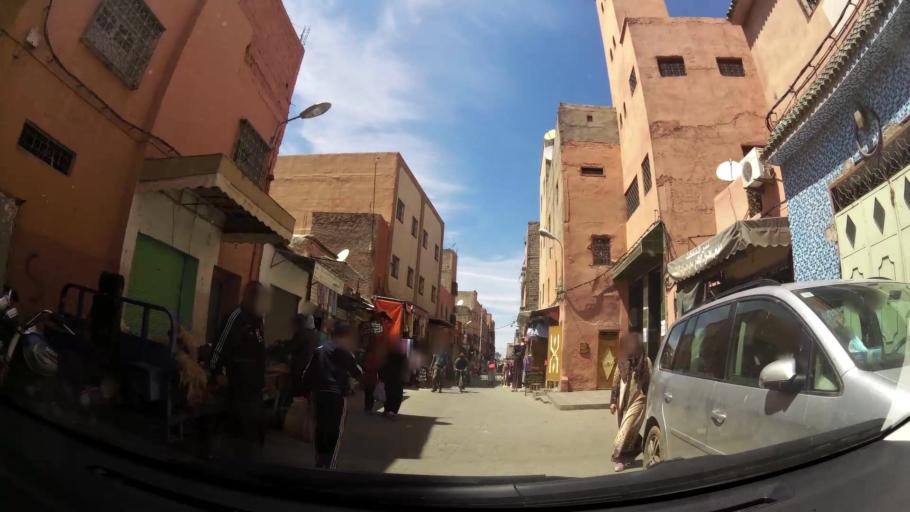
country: MA
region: Marrakech-Tensift-Al Haouz
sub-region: Marrakech
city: Marrakesh
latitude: 31.6187
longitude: -7.9702
